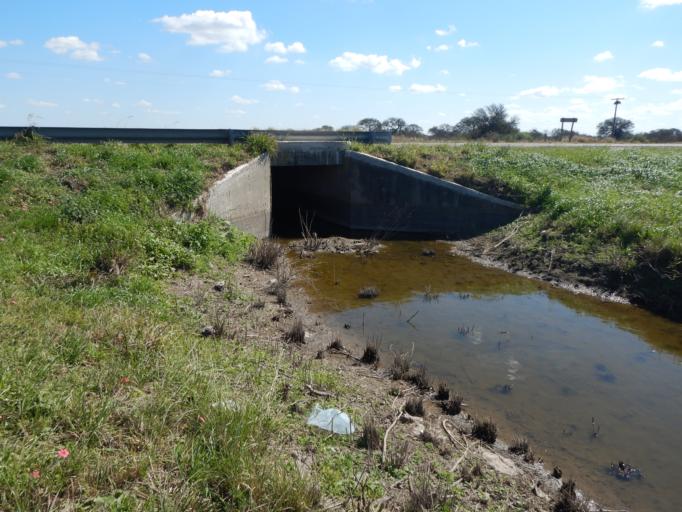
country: AR
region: Santiago del Estero
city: Los Juries
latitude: -28.6667
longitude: -61.5295
